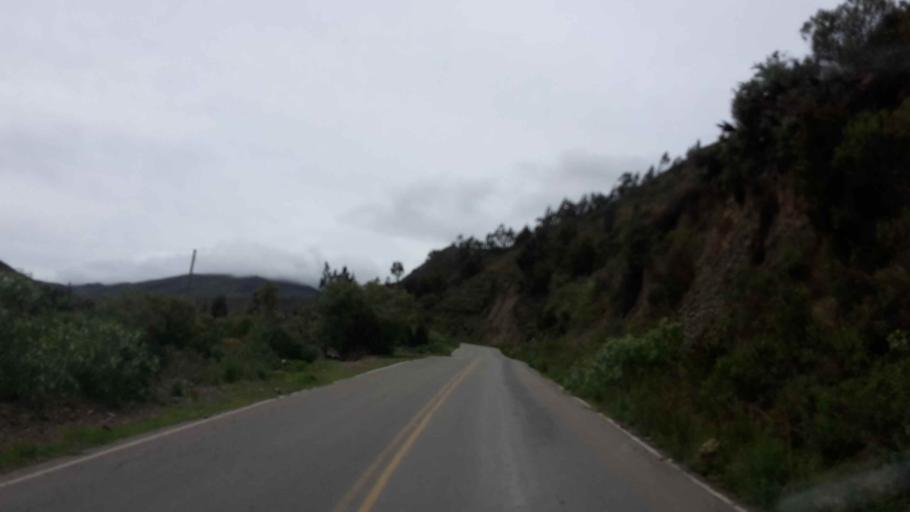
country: BO
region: Cochabamba
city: Colomi
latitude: -17.4030
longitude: -65.7920
